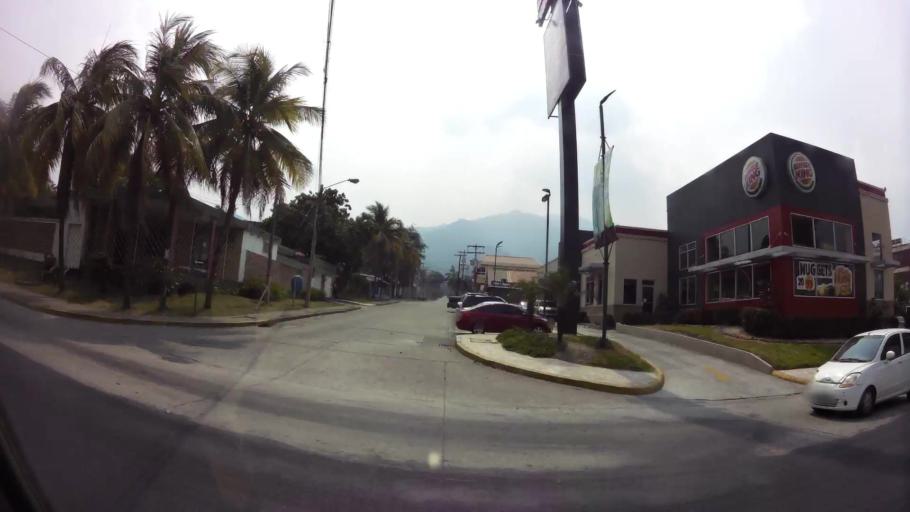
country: HN
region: Cortes
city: San Pedro Sula
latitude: 15.5051
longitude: -88.0375
